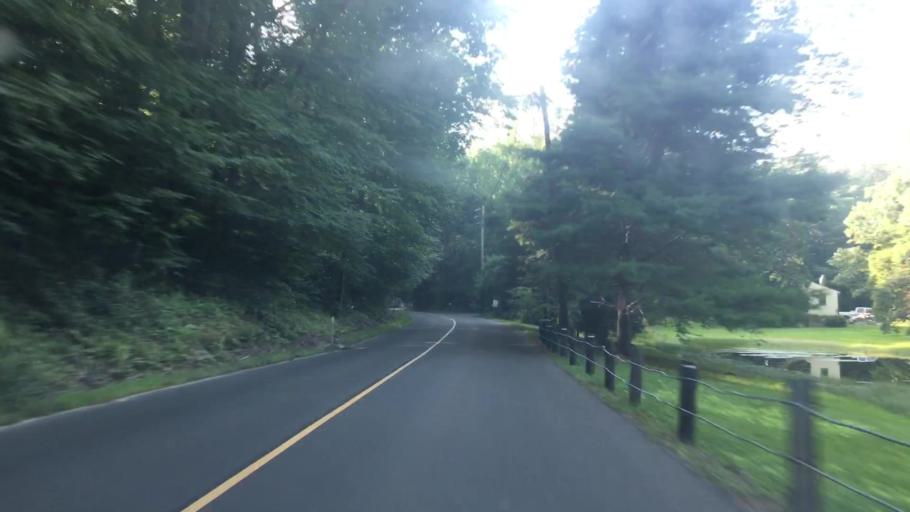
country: US
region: Connecticut
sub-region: Middlesex County
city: Chester Center
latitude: 41.3949
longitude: -72.4518
